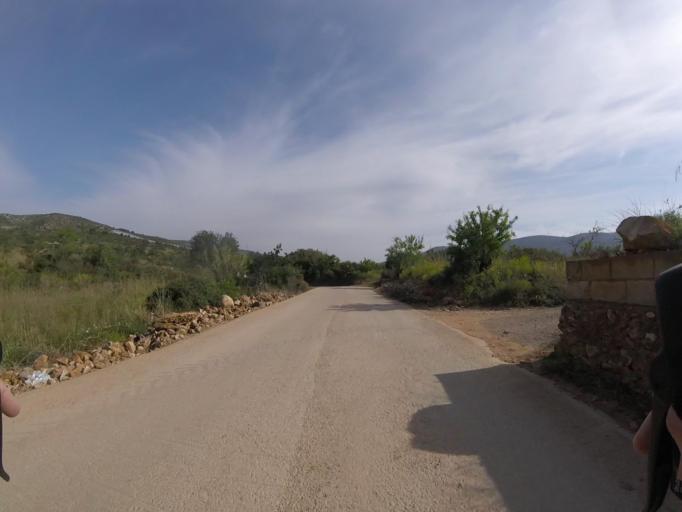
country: ES
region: Valencia
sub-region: Provincia de Castello
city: Alcala de Xivert
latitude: 40.2690
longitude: 0.2524
